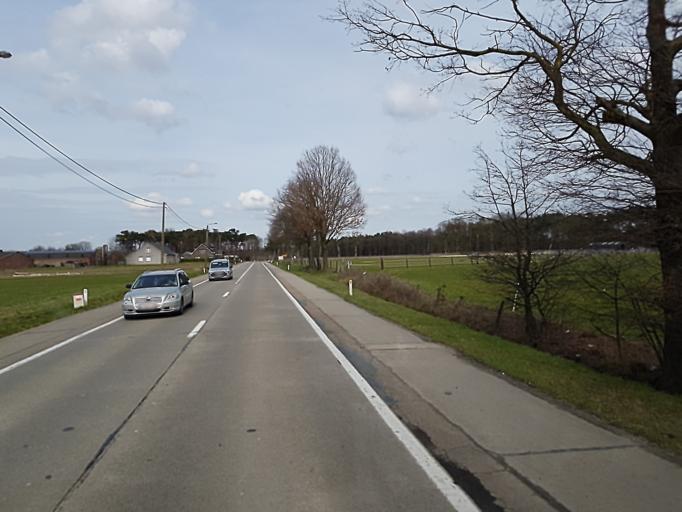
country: BE
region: Flanders
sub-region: Provincie Antwerpen
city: Meerhout
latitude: 51.1580
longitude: 5.0989
